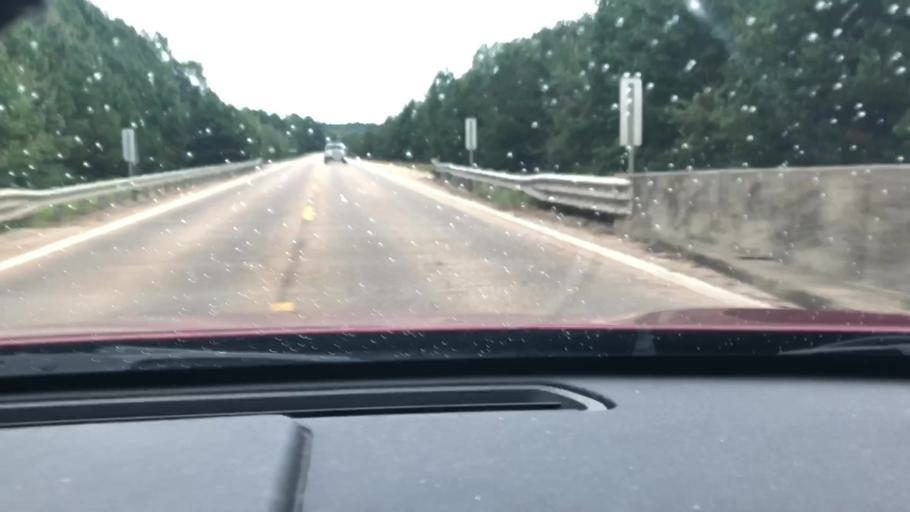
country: US
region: Arkansas
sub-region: Lafayette County
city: Stamps
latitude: 33.3670
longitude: -93.5220
